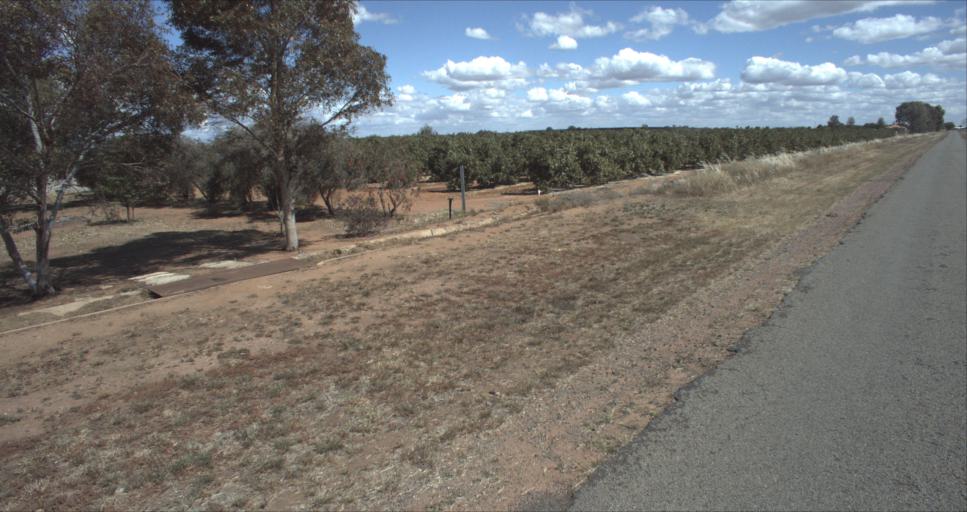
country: AU
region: New South Wales
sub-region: Leeton
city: Leeton
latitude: -34.5136
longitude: 146.2405
